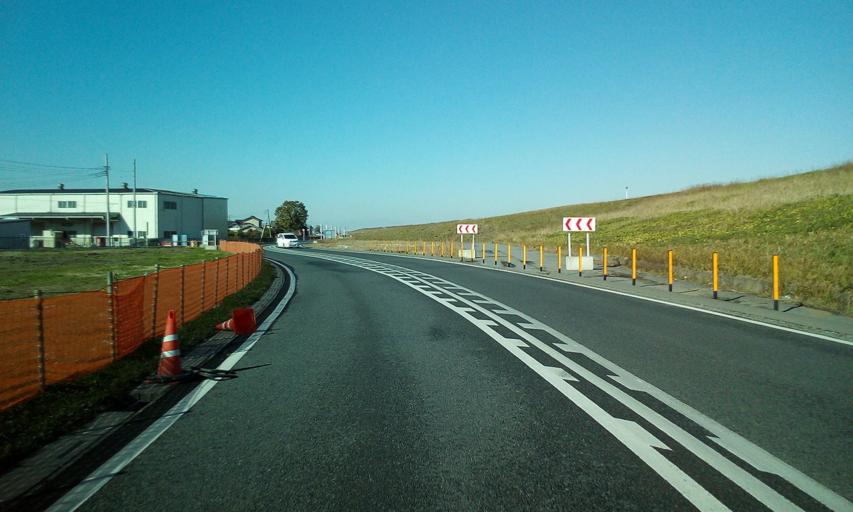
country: JP
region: Chiba
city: Noda
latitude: 35.9287
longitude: 139.8593
